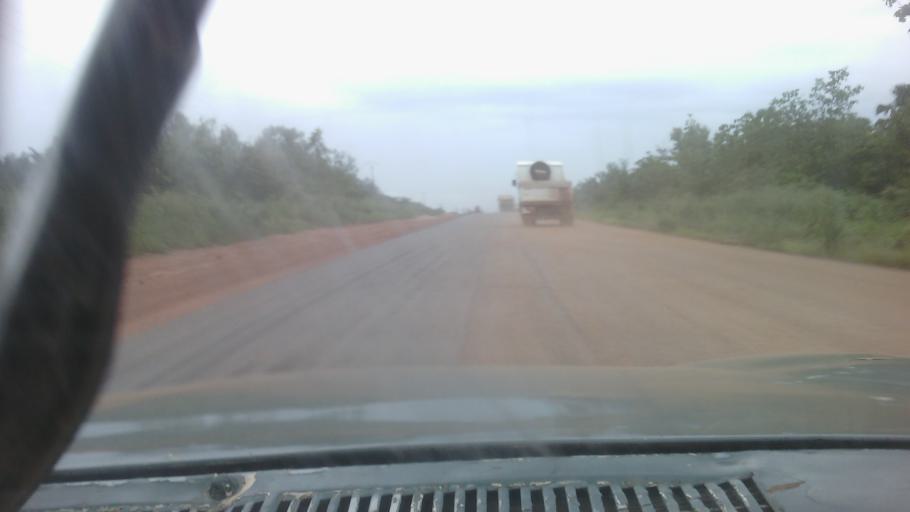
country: BJ
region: Mono
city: Come
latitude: 6.5024
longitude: 1.8353
